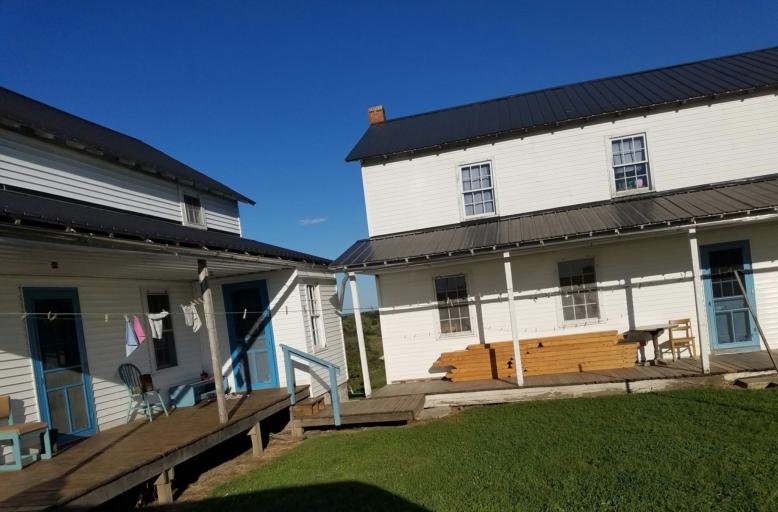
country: US
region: Iowa
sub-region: Decatur County
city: Lamoni
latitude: 40.6522
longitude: -93.9164
